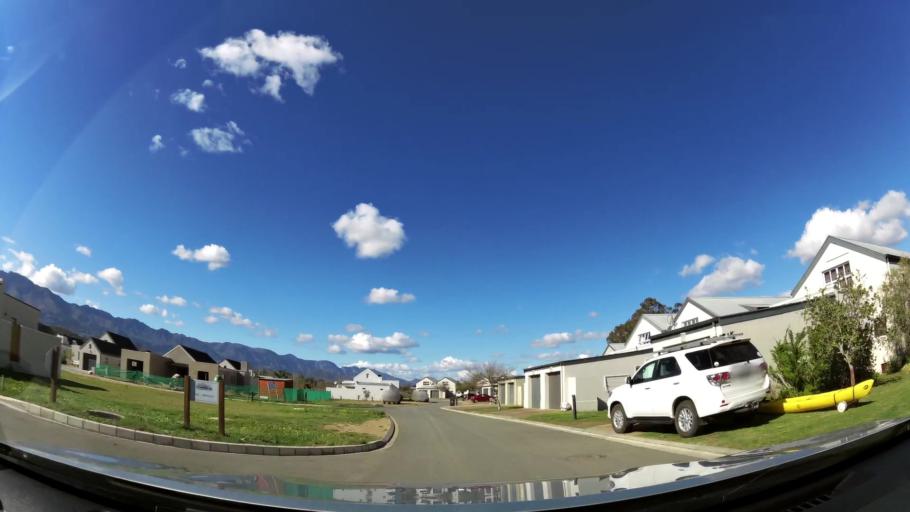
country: ZA
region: Western Cape
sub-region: Cape Winelands District Municipality
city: Ashton
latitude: -33.8122
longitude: 19.8562
